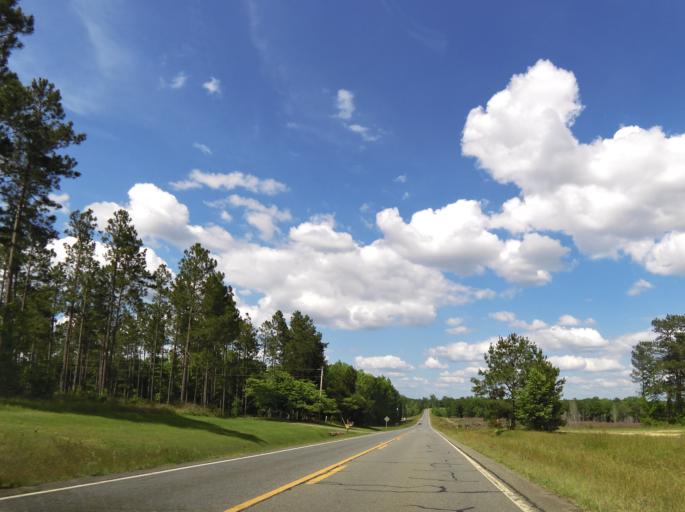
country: US
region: Georgia
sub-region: Treutlen County
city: Soperton
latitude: 32.3405
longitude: -82.6527
